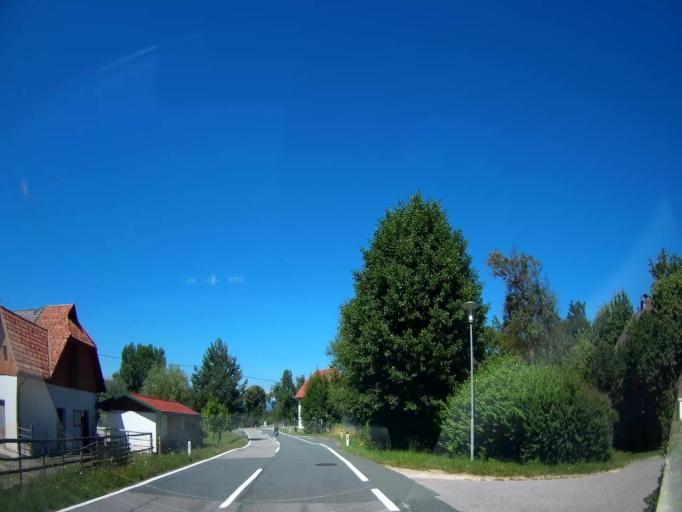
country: AT
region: Carinthia
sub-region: Politischer Bezirk Volkermarkt
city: Gallizien
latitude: 46.5496
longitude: 14.4728
